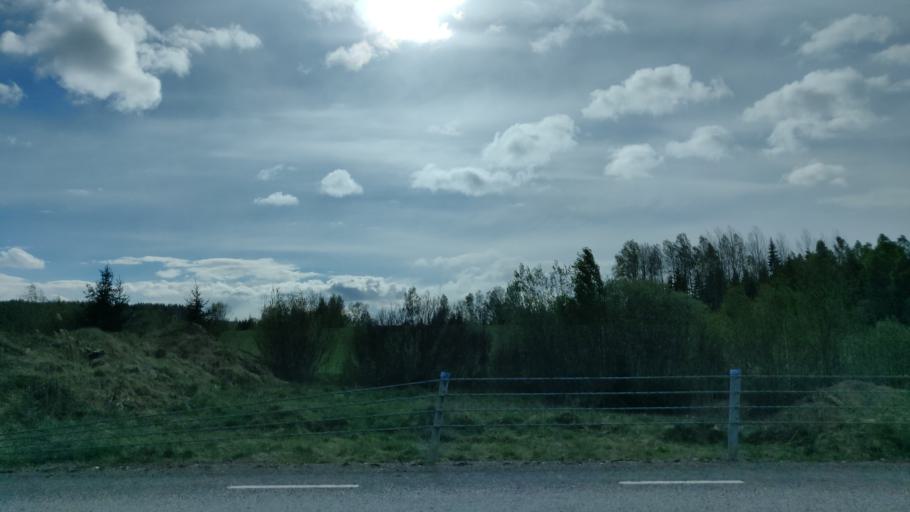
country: SE
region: Vaermland
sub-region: Forshaga Kommun
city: Deje
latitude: 59.5770
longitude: 13.4694
